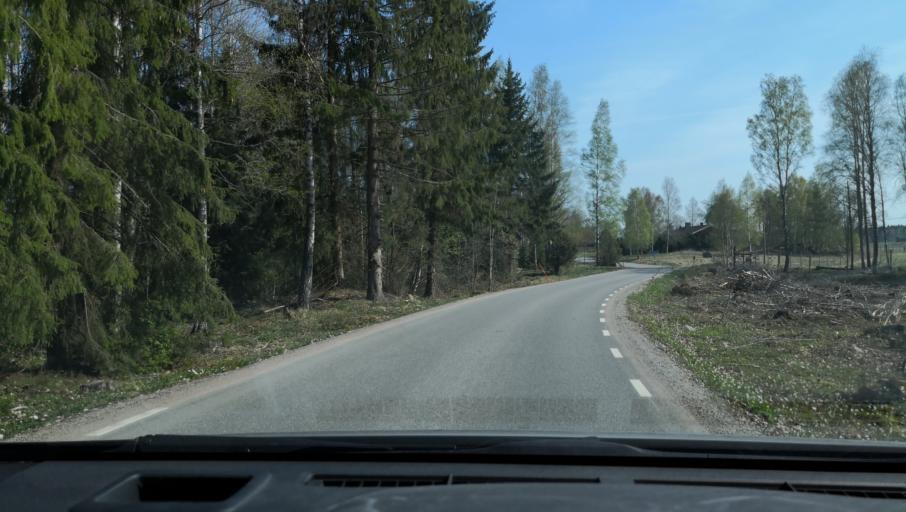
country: SE
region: Vaestmanland
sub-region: Sala Kommun
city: Sala
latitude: 60.0091
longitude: 16.6875
